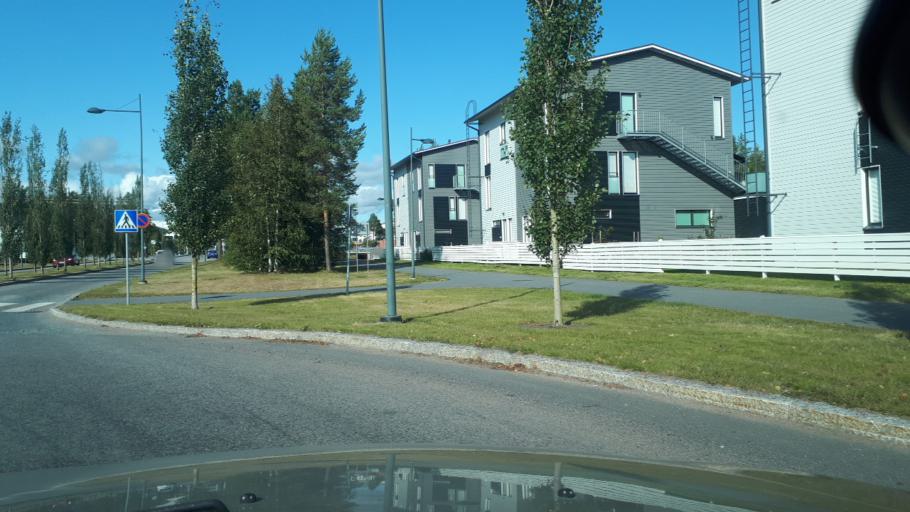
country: FI
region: Northern Ostrobothnia
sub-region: Oulu
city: Oulu
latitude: 65.0768
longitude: 25.4519
